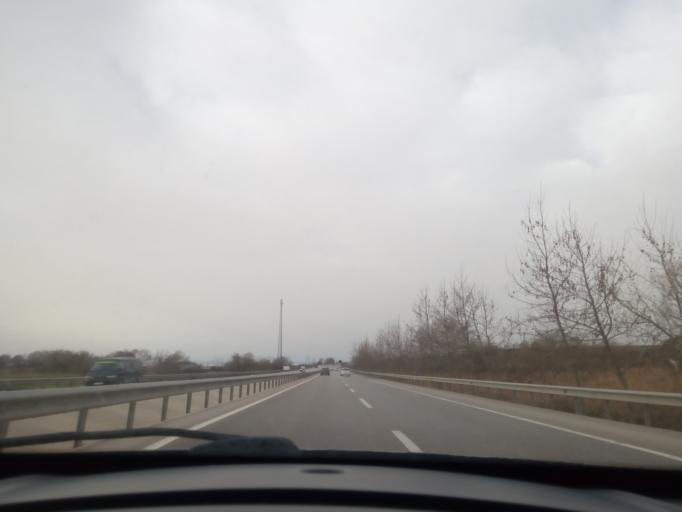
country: TR
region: Bursa
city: Mahmudiye
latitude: 40.2110
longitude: 28.6094
